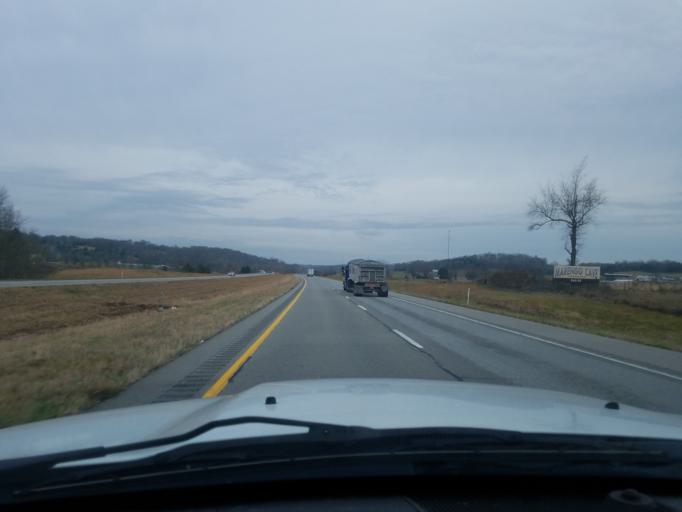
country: US
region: Indiana
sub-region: Harrison County
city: Corydon
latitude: 38.2422
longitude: -86.1763
